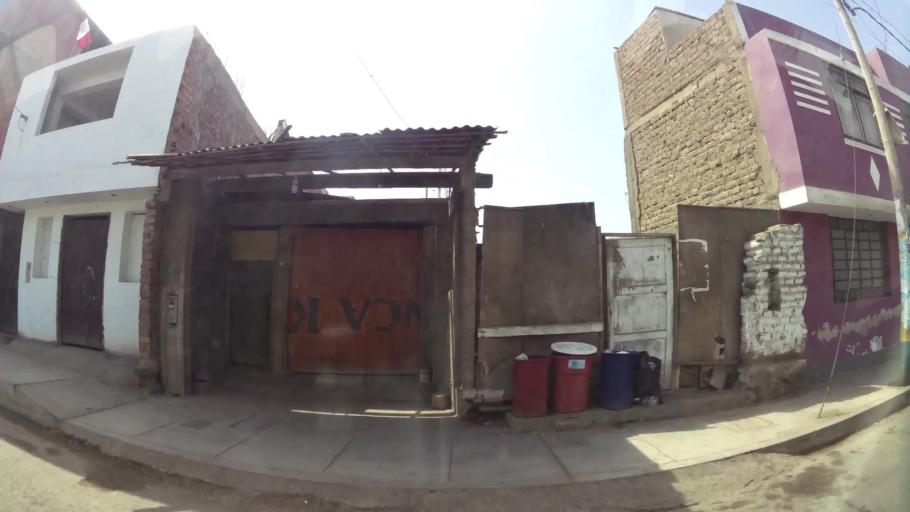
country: PE
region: Lima
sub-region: Provincia de Canete
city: Mala
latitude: -12.6572
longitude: -76.6312
